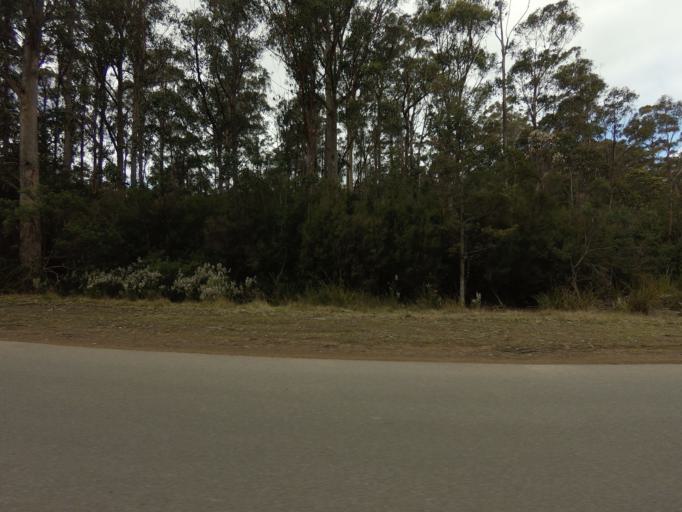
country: AU
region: Tasmania
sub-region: Huon Valley
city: Geeveston
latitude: -43.3647
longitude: 146.9591
